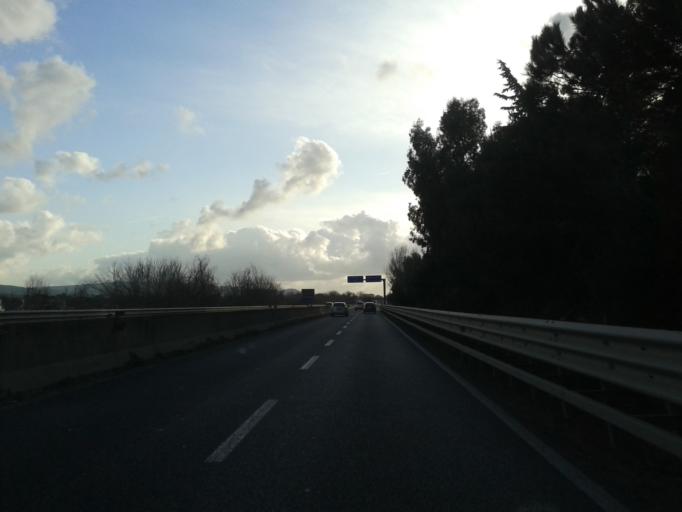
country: IT
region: Tuscany
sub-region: Provincia di Livorno
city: Livorno
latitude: 43.5597
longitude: 10.3454
